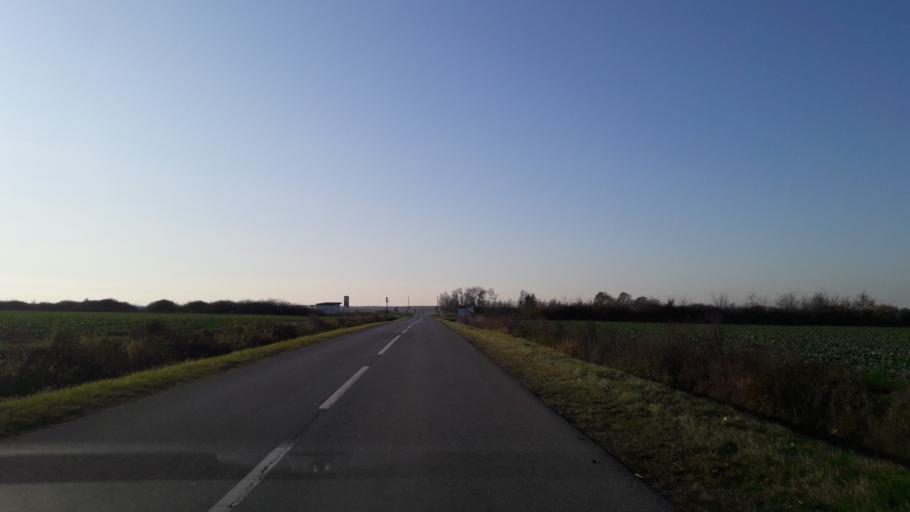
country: HR
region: Osjecko-Baranjska
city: Vuka
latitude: 45.4217
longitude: 18.5268
